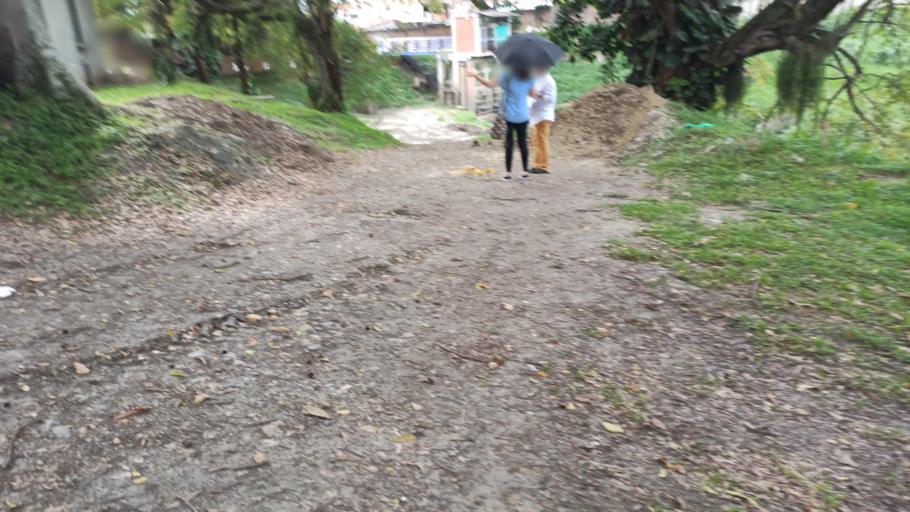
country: CO
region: Valle del Cauca
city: Palmira
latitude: 3.5287
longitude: -76.2879
